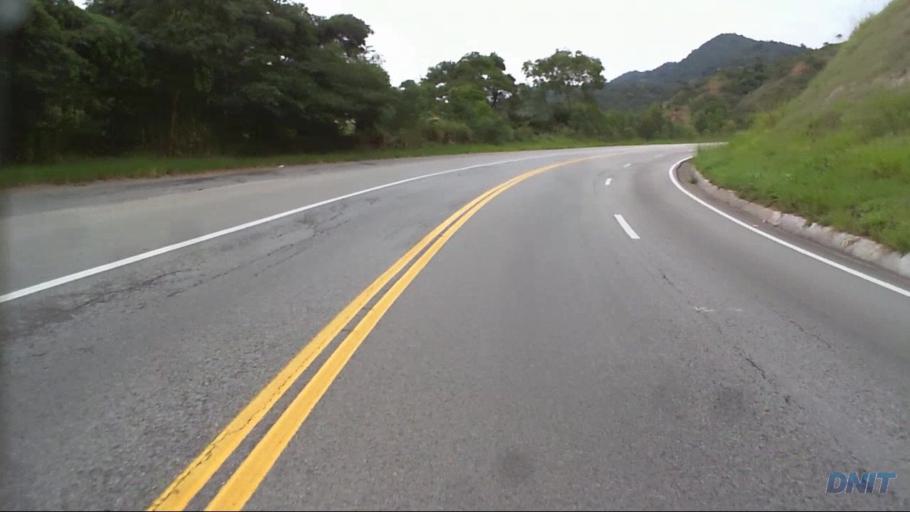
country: BR
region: Minas Gerais
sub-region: Nova Era
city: Nova Era
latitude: -19.6265
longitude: -42.8703
